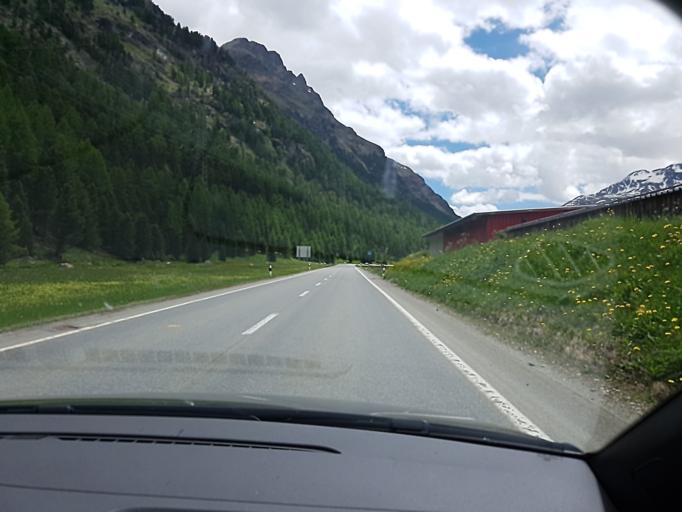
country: CH
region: Grisons
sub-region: Maloja District
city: Pontresina
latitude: 46.4805
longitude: 9.9168
